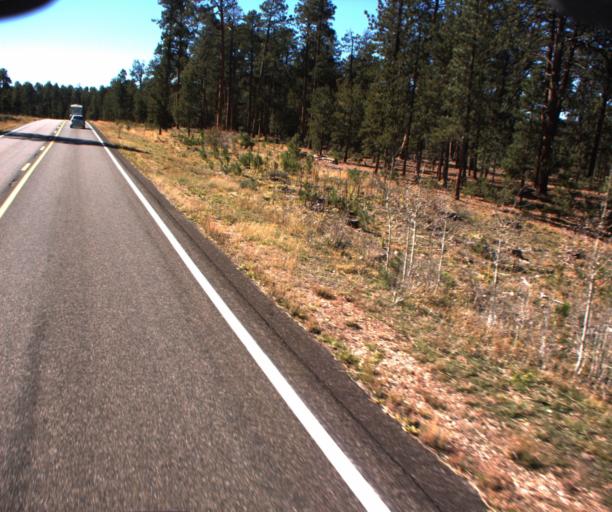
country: US
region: Arizona
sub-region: Coconino County
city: Fredonia
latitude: 36.6897
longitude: -112.2168
